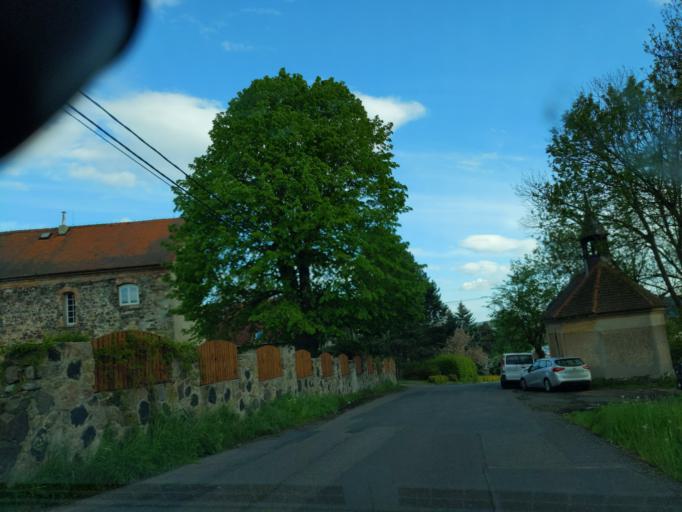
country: CZ
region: Ustecky
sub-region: Okres Usti nad Labem
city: Usti nad Labem
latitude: 50.7039
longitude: 14.0022
